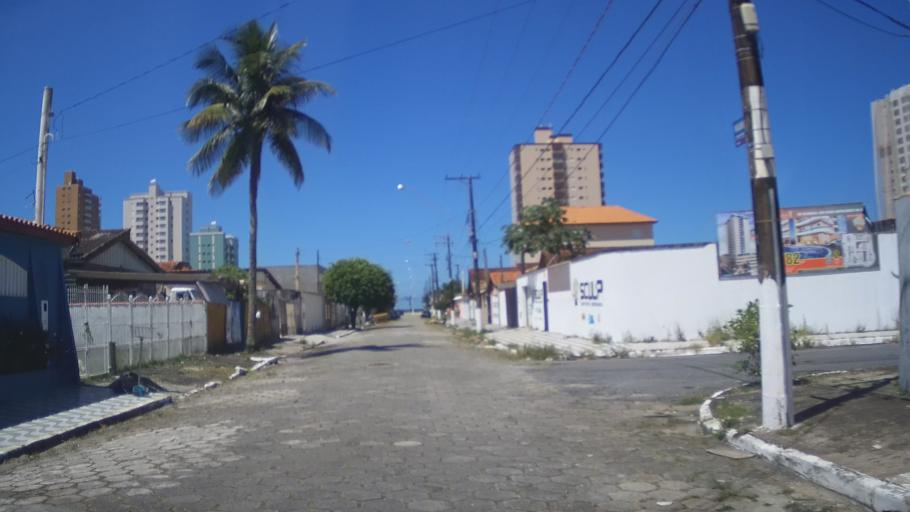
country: BR
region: Sao Paulo
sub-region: Mongagua
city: Mongagua
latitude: -24.0447
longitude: -46.5173
